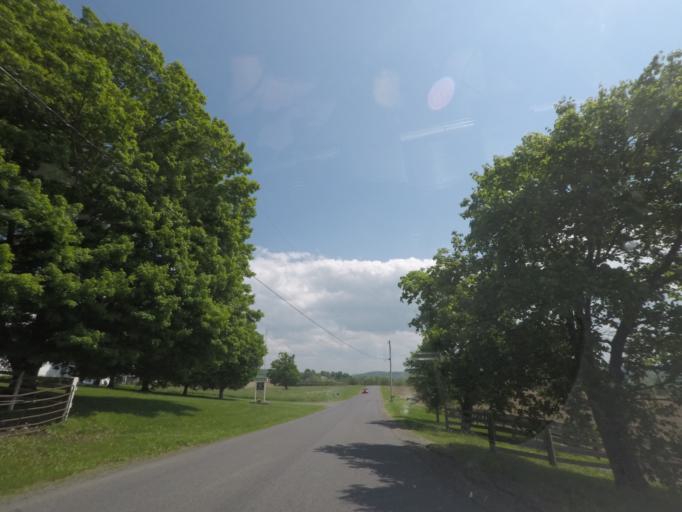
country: US
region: New York
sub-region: Dutchess County
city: Pine Plains
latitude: 41.9800
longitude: -73.5506
